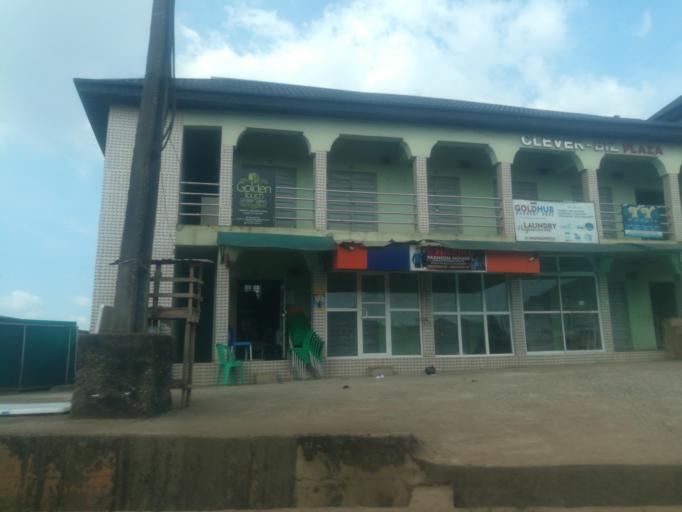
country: NG
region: Ogun
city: Abeokuta
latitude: 7.1181
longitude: 3.3225
